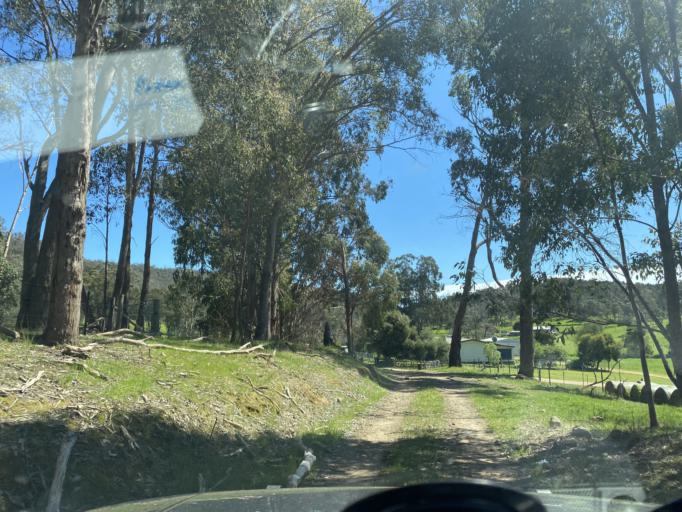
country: AU
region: Victoria
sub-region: Benalla
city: Benalla
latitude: -36.7126
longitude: 146.1820
